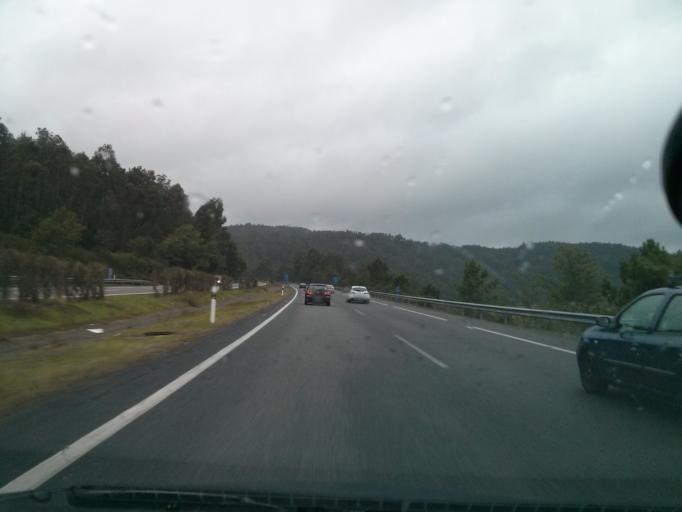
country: ES
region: Galicia
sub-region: Provincia de Pontevedra
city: Porrino
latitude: 42.1771
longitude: -8.5615
